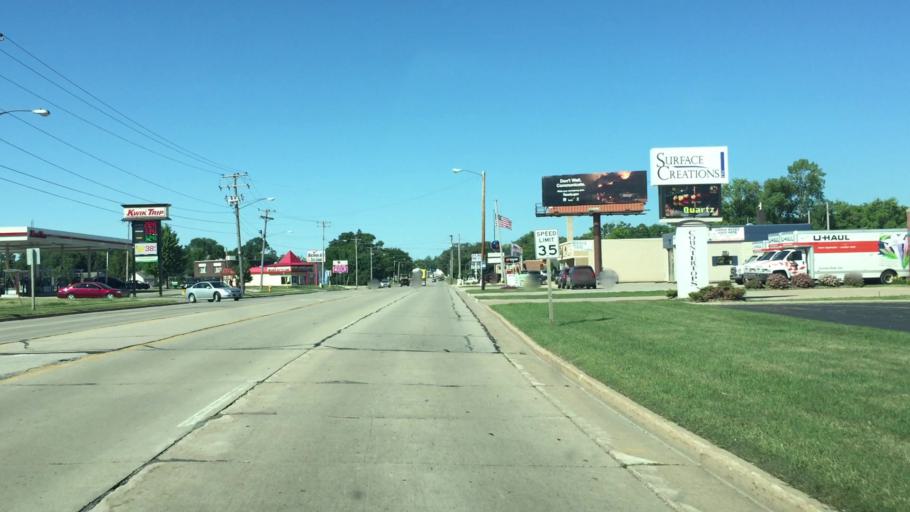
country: US
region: Wisconsin
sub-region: Outagamie County
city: Appleton
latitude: 44.2420
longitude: -88.4168
